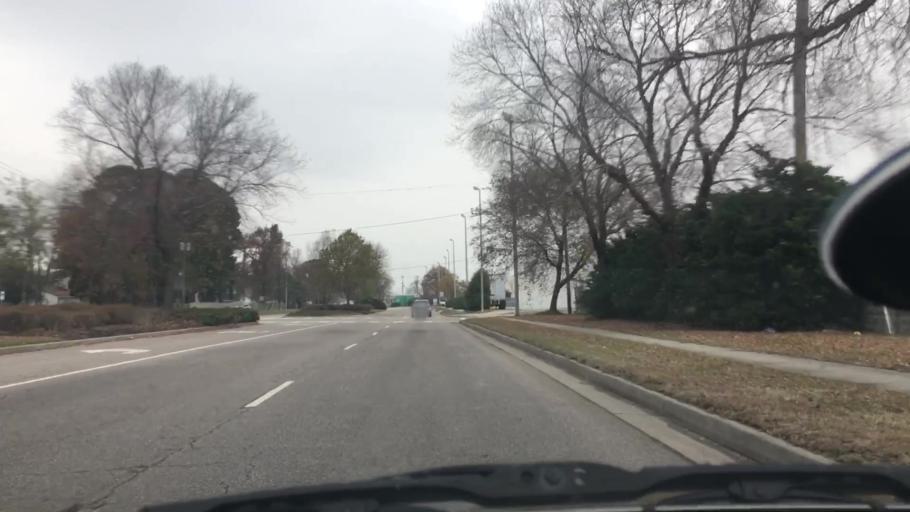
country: US
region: Virginia
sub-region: City of Norfolk
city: Norfolk
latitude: 36.8711
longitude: -76.2507
